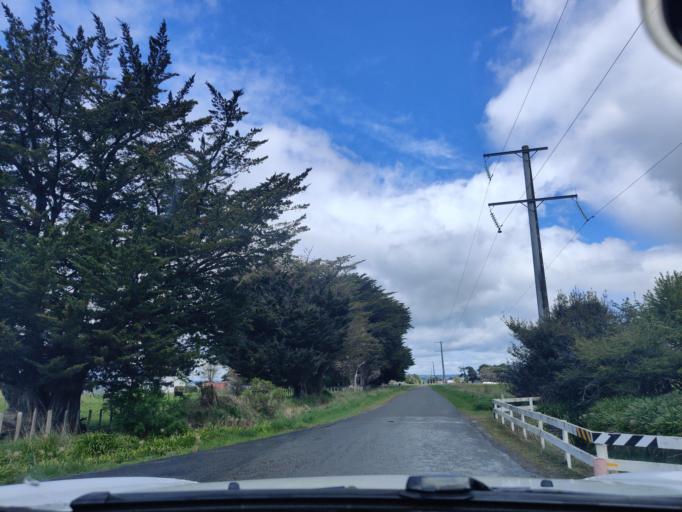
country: NZ
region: Manawatu-Wanganui
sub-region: Palmerston North City
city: Palmerston North
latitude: -40.3066
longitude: 175.8600
